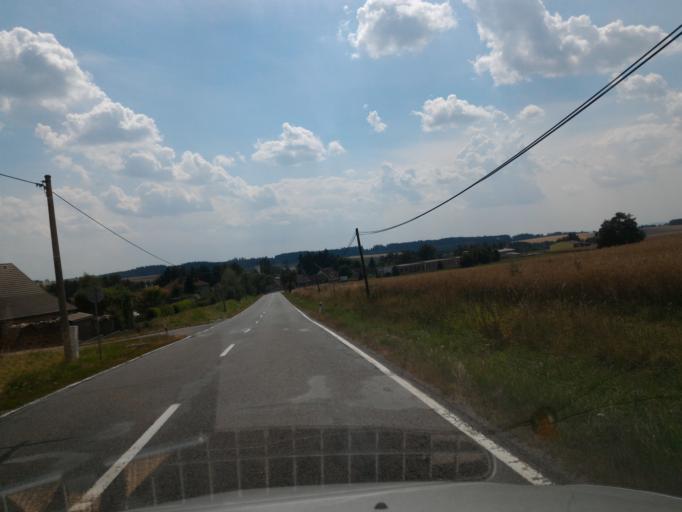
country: CZ
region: Vysocina
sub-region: Okres Jihlava
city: Polna
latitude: 49.4483
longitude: 15.7773
